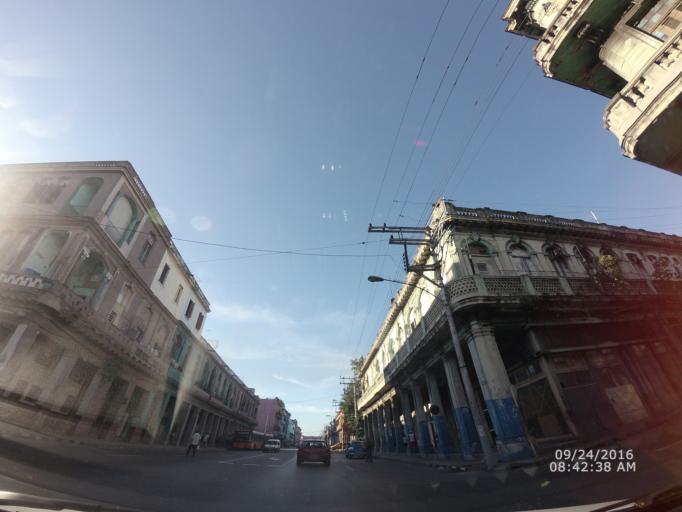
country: CU
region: La Habana
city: Havana
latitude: 23.1364
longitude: -82.3784
